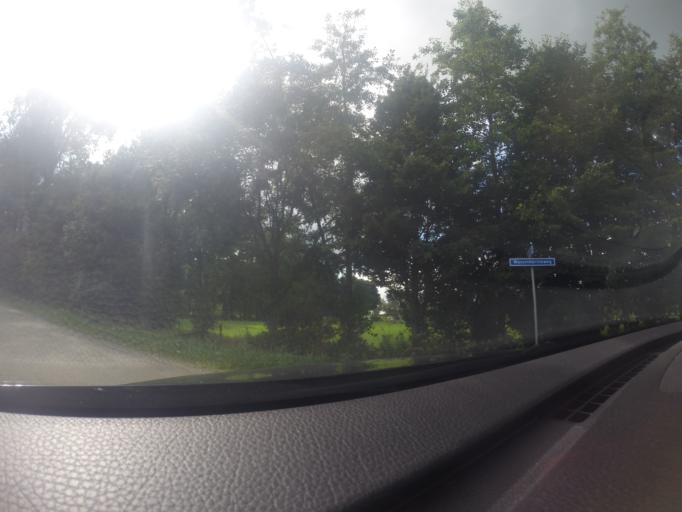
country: NL
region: Gelderland
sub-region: Gemeente Bronckhorst
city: Zelhem
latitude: 51.9904
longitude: 6.3274
